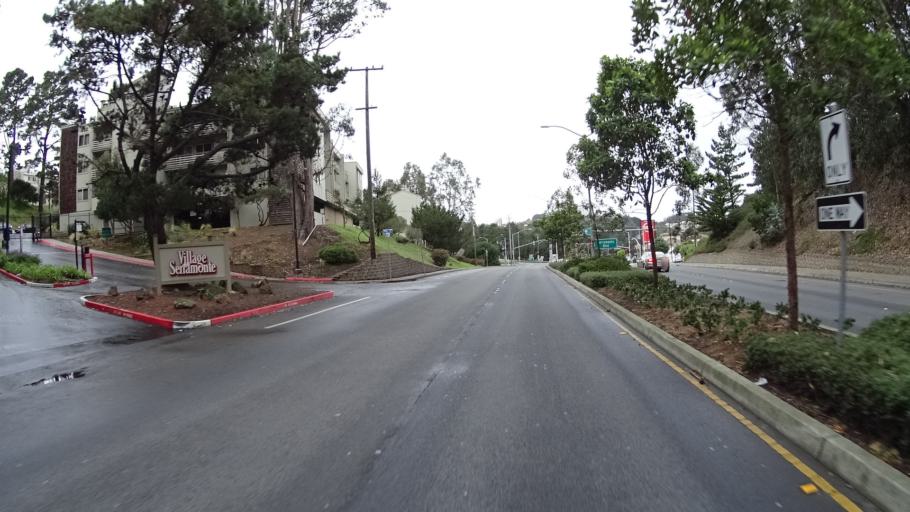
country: US
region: California
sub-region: San Mateo County
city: Colma
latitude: 37.6695
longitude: -122.4631
